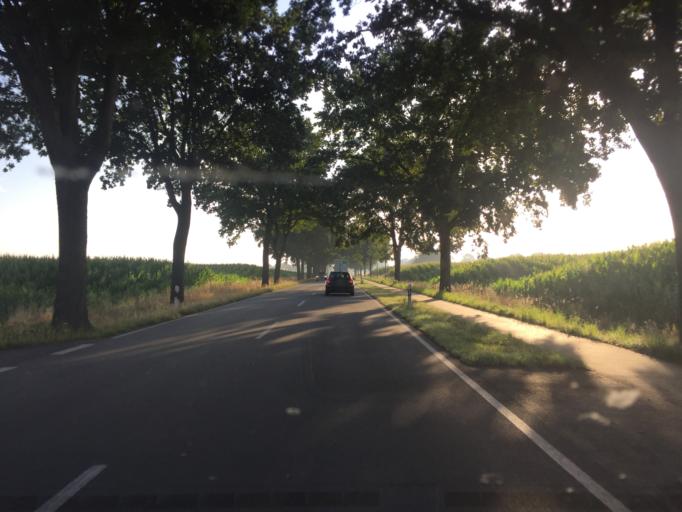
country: DE
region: Lower Saxony
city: Bohme
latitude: 52.8228
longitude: 9.4645
